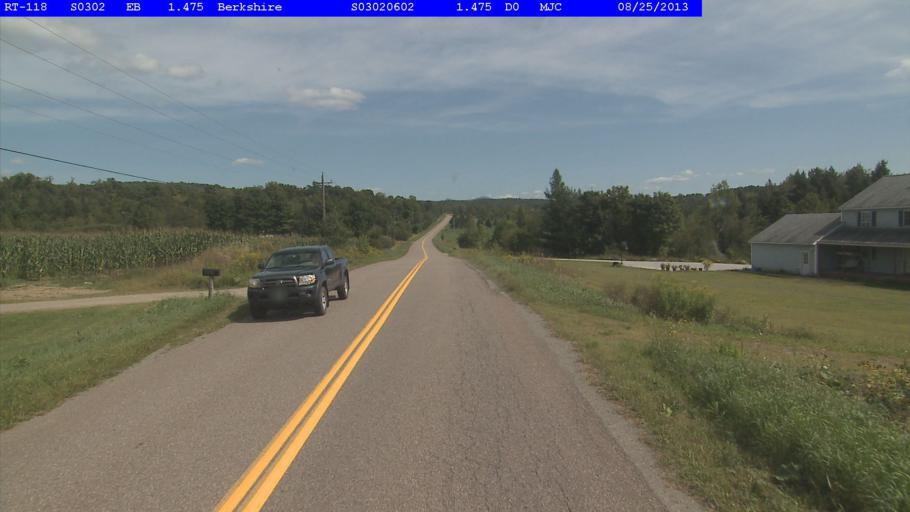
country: US
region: Vermont
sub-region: Franklin County
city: Enosburg Falls
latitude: 44.9799
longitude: -72.7875
